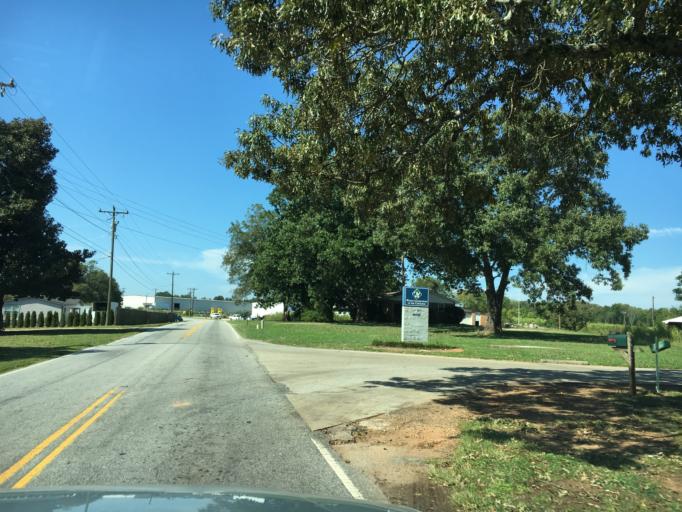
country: US
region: South Carolina
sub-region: Spartanburg County
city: Duncan
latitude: 34.8910
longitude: -82.1420
